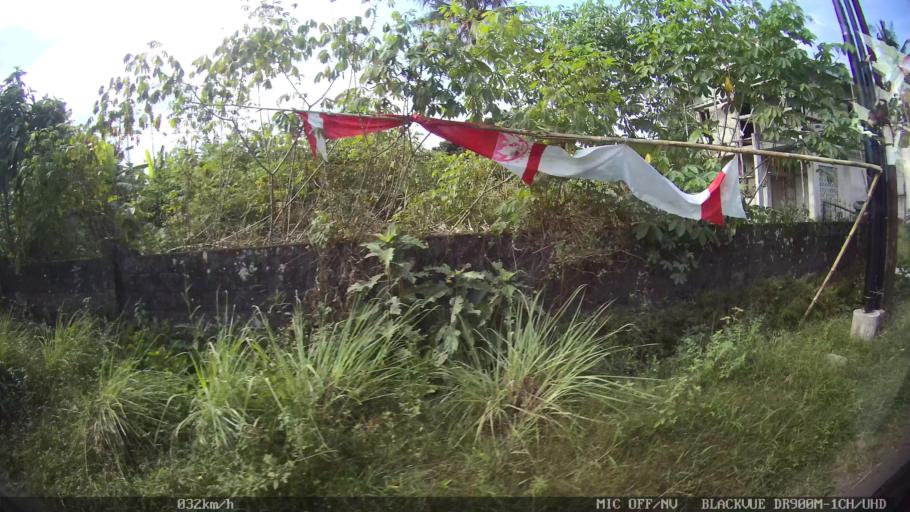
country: ID
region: Daerah Istimewa Yogyakarta
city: Depok
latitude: -7.7282
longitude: 110.4157
